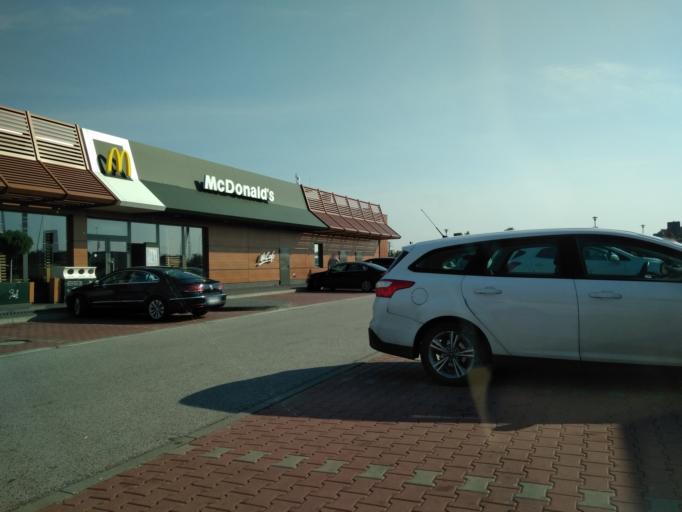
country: PL
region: Lodz Voivodeship
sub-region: powiat Lowicki
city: Bobrowniki
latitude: 52.0290
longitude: 20.0019
